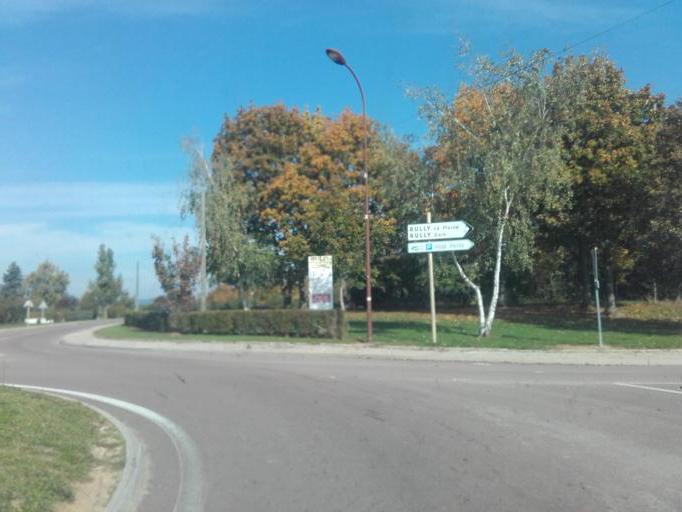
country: FR
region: Bourgogne
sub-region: Departement de Saone-et-Loire
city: Rully
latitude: 46.8792
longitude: 4.7526
